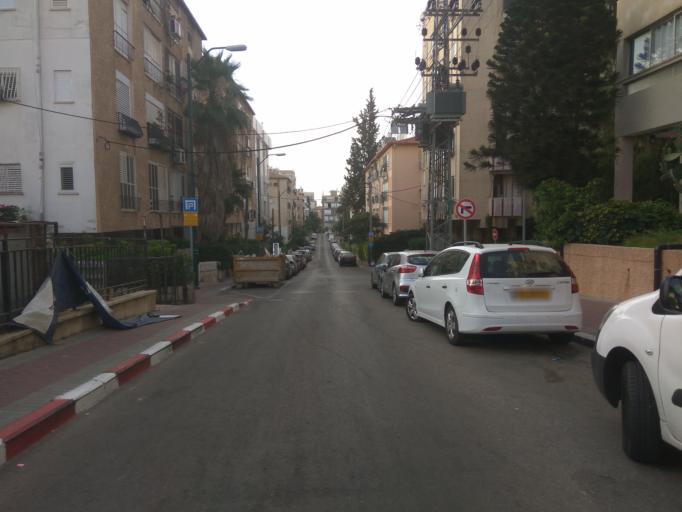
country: IL
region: Central District
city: Rishon LeZiyyon
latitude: 31.9645
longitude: 34.8061
